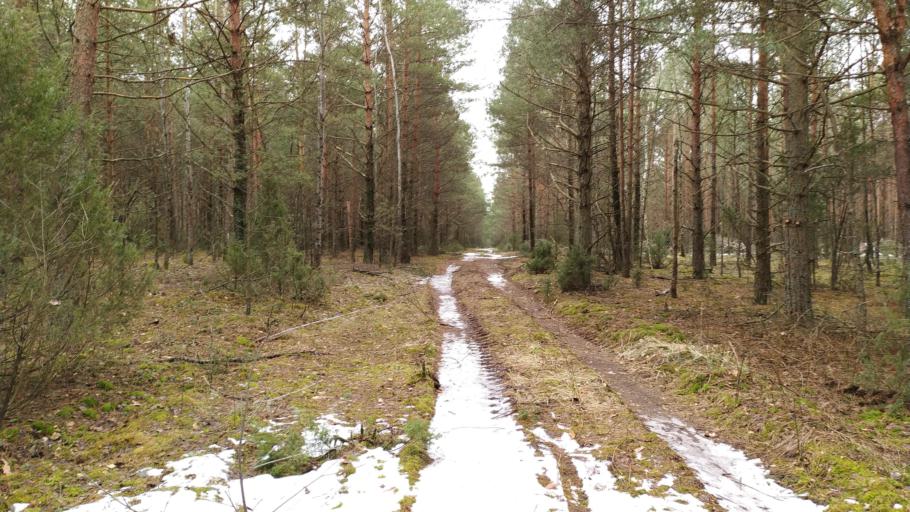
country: BY
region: Brest
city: Kamyanyets
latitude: 52.4348
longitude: 23.9997
